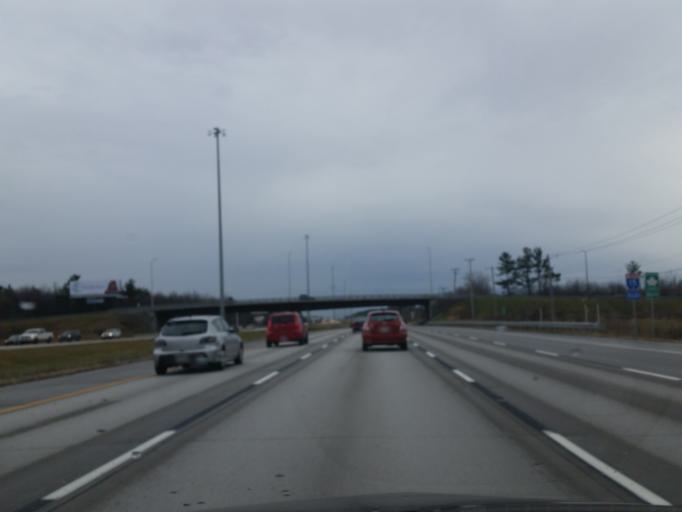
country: CA
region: Quebec
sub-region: Laurentides
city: Blainville
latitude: 45.6774
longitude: -73.9146
